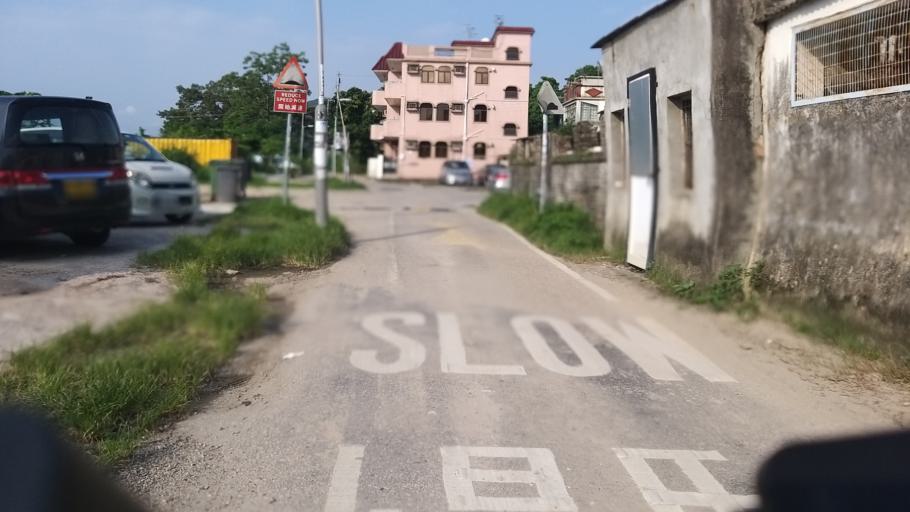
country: HK
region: Yuen Long
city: Yuen Long Kau Hui
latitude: 22.4530
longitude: 114.0374
